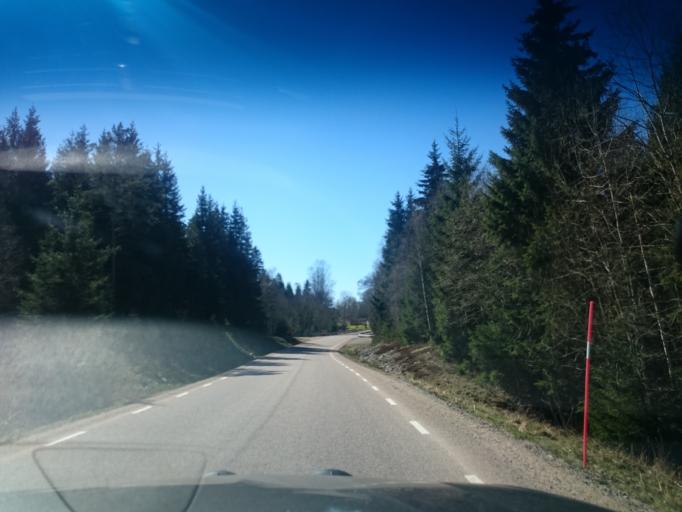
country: SE
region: Kronoberg
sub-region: Vaxjo Kommun
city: Braas
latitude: 57.2354
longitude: 15.0321
